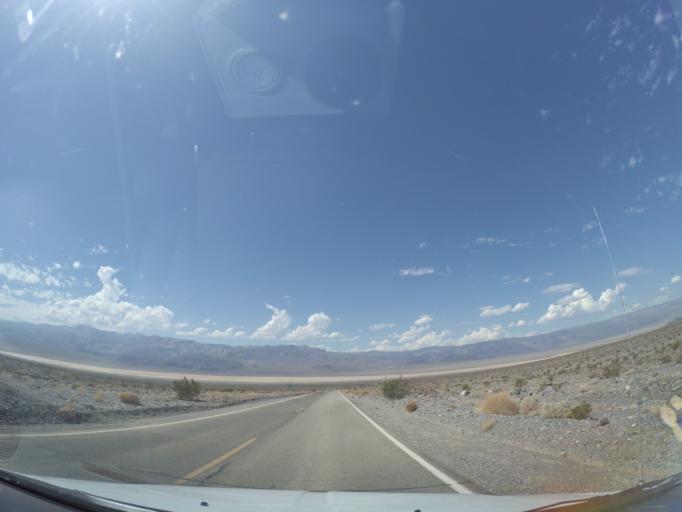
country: US
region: California
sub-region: San Bernardino County
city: Searles Valley
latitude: 36.3447
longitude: -117.3559
